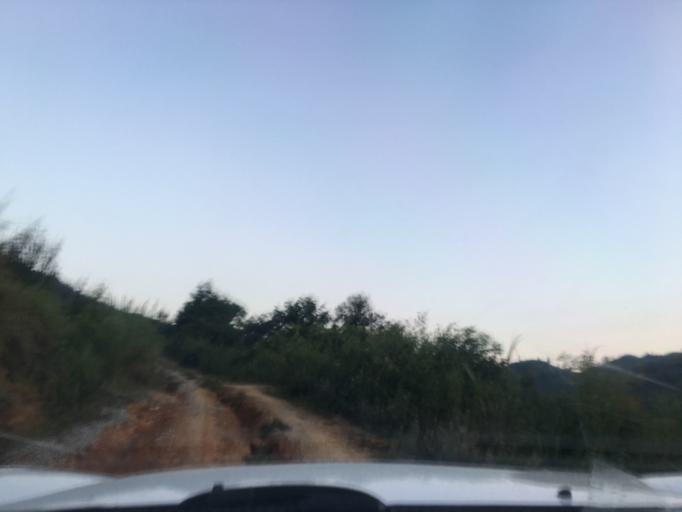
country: CN
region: Guangxi Zhuangzu Zizhiqu
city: Xinzhou
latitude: 25.3506
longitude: 105.7389
